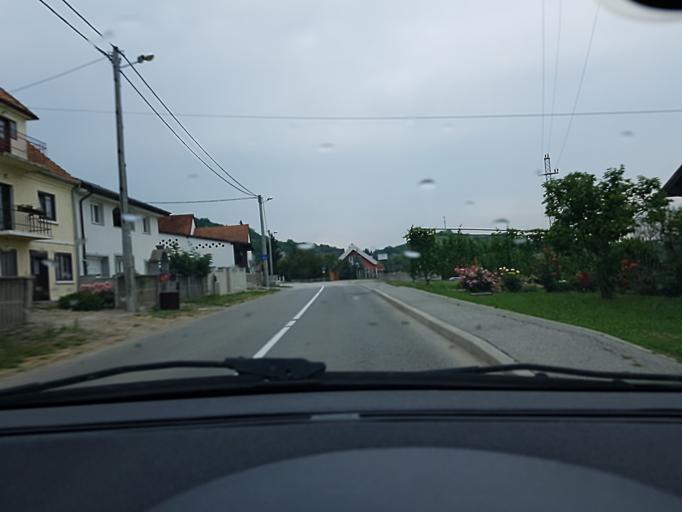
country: HR
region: Zagrebacka
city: Pojatno
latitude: 45.9173
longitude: 15.8077
